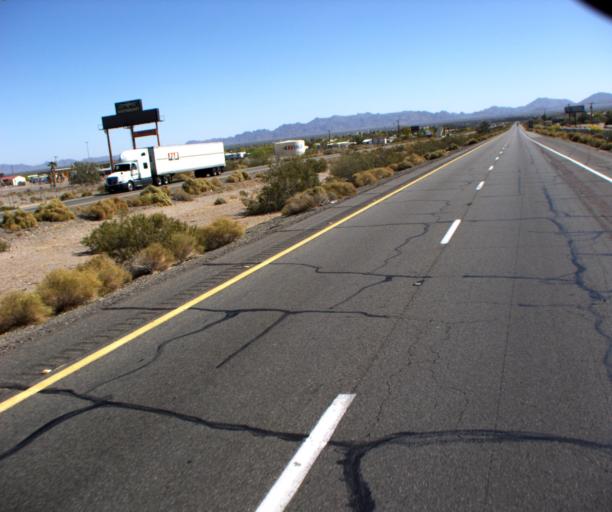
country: US
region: Arizona
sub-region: La Paz County
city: Quartzsite
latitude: 33.6605
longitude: -114.2347
